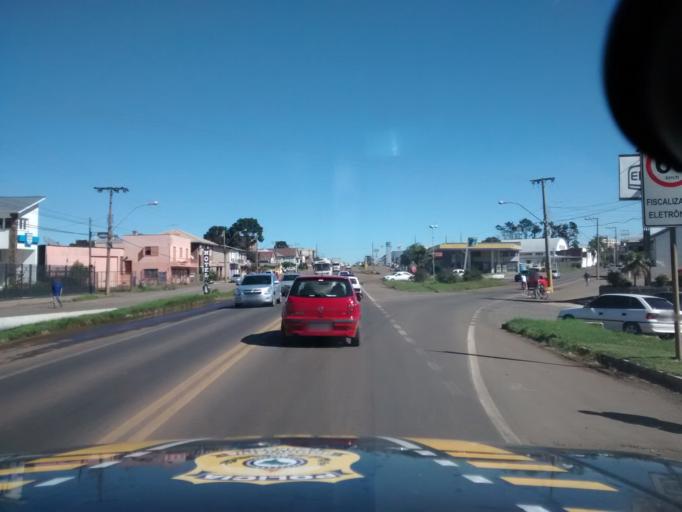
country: BR
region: Rio Grande do Sul
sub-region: Vacaria
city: Vacaria
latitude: -28.5086
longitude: -50.9287
